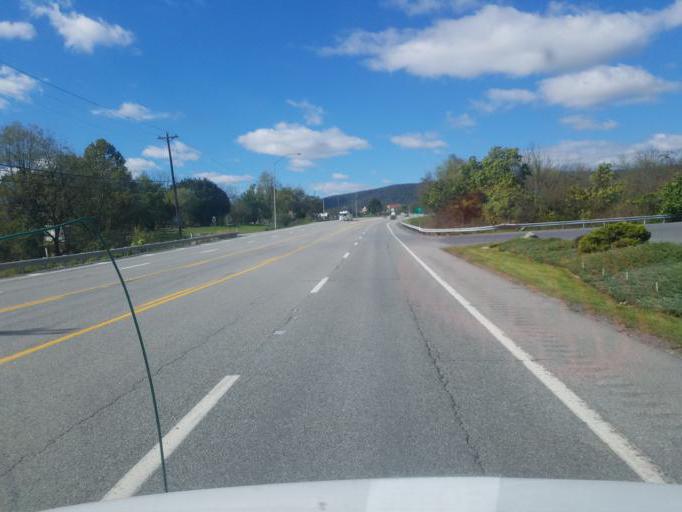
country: US
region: Pennsylvania
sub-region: Bedford County
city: Earlston
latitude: 40.0200
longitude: -78.3460
